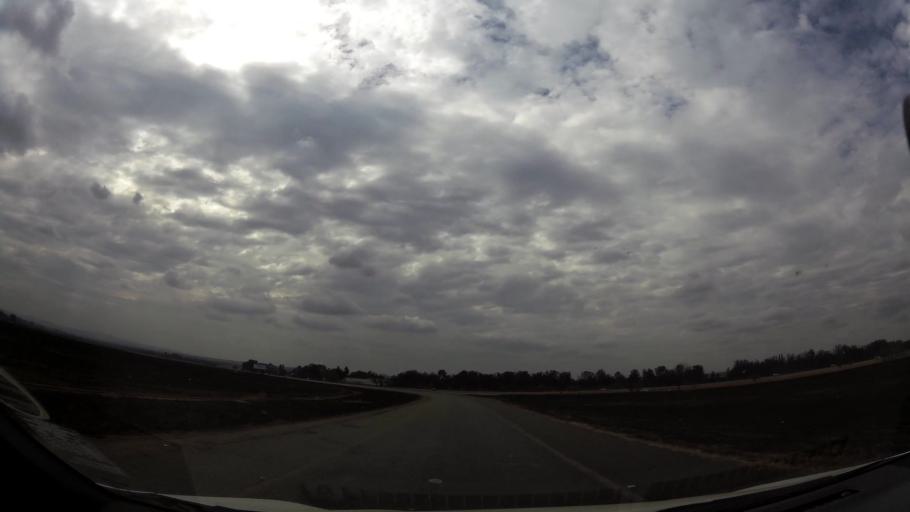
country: ZA
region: Gauteng
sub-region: Sedibeng District Municipality
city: Meyerton
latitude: -26.4153
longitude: 28.0763
